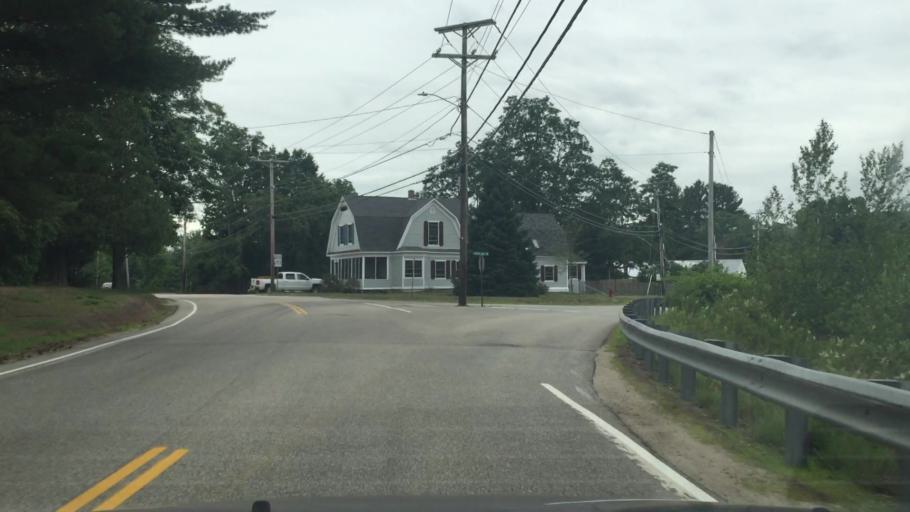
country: US
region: New Hampshire
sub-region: Carroll County
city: Conway
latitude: 43.9742
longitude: -71.1169
